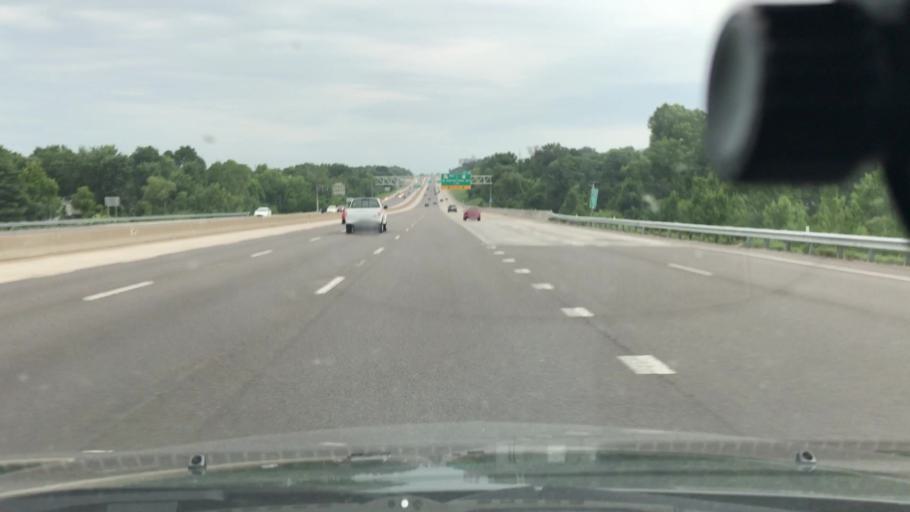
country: US
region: Missouri
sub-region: Saint Louis County
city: Creve Coeur
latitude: 38.6775
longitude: -90.4493
